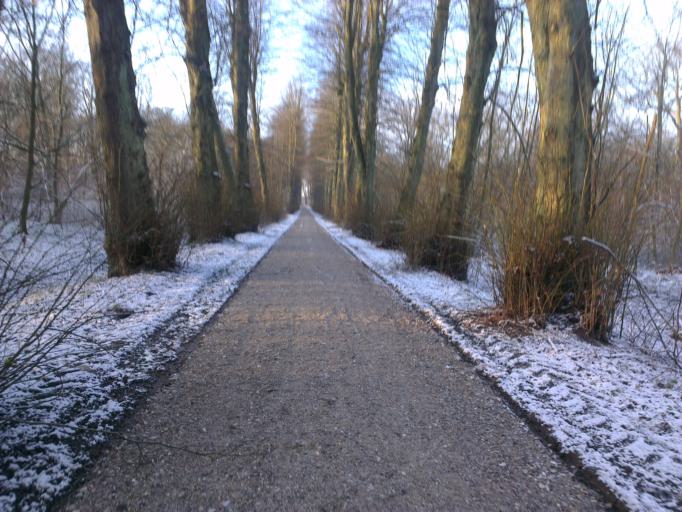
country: DK
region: Capital Region
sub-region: Frederikssund Kommune
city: Jaegerspris
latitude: 55.8598
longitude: 11.9784
